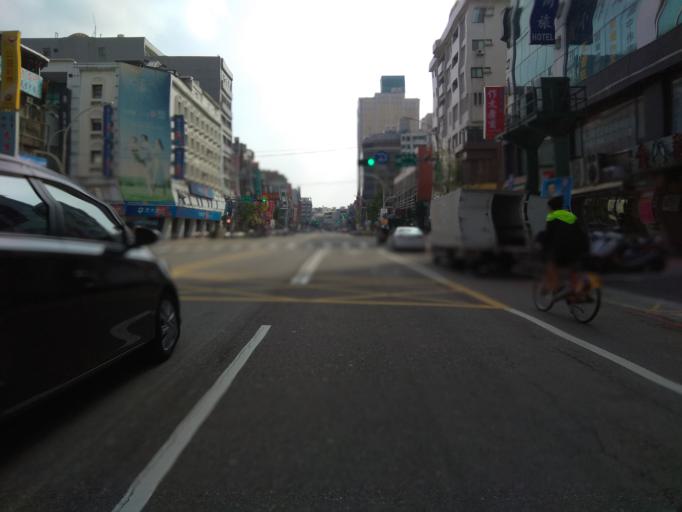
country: TW
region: Taiwan
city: Taoyuan City
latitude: 24.9574
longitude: 121.2233
